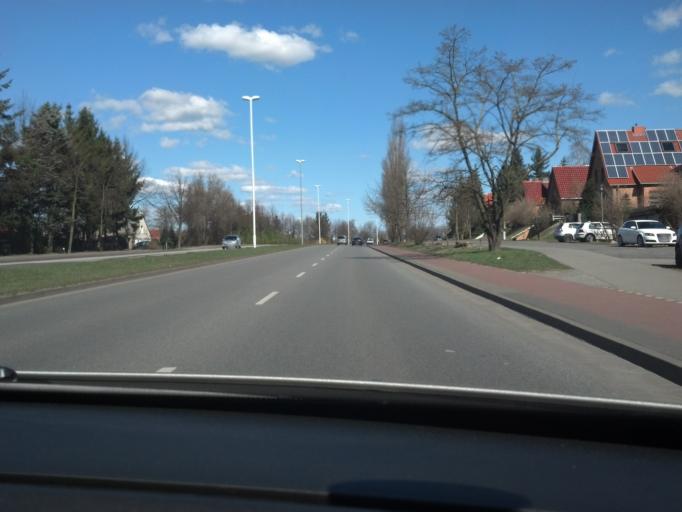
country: DE
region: Mecklenburg-Vorpommern
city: Neubrandenburg
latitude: 53.5724
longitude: 13.2692
